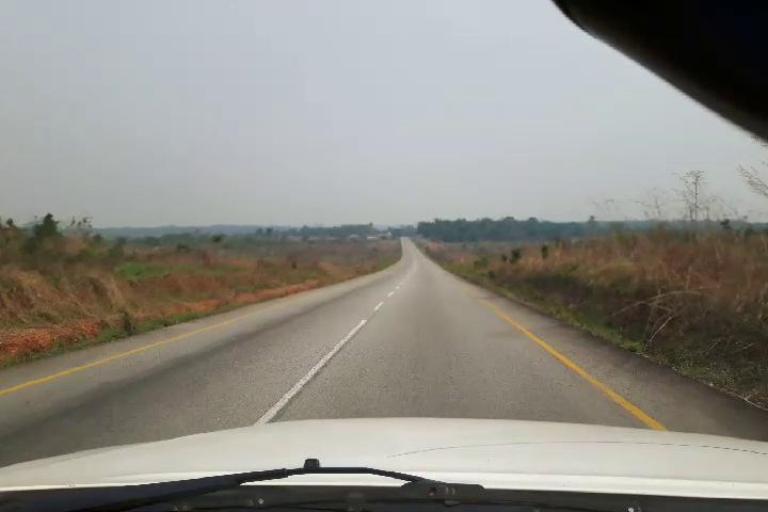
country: SL
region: Southern Province
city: Largo
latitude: 8.2256
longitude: -12.0763
